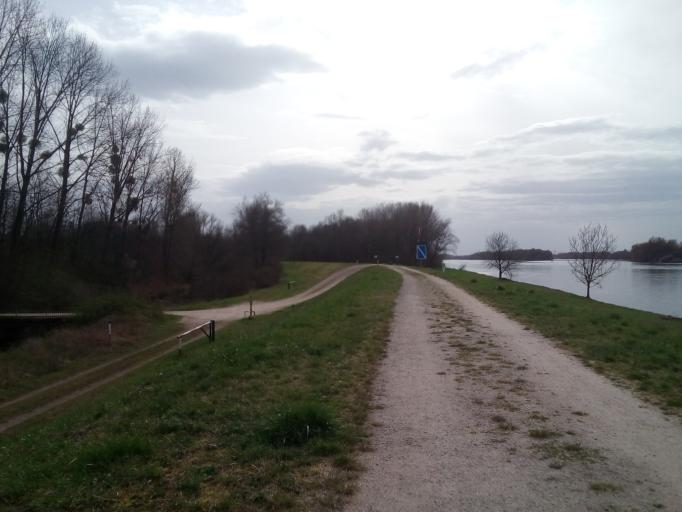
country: DE
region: Baden-Wuerttemberg
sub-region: Freiburg Region
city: Rheinau
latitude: 48.7084
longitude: 7.9496
